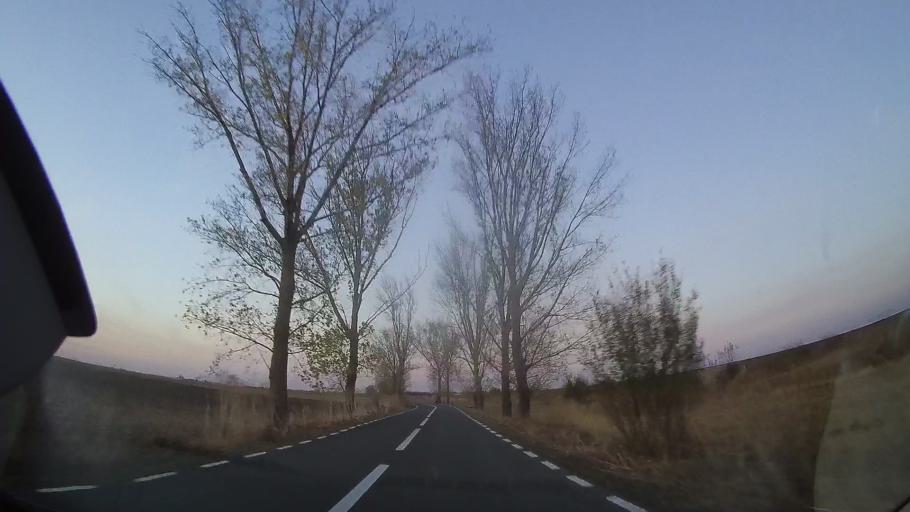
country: RO
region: Constanta
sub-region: Comuna Cobadin
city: Cobadin
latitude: 44.0388
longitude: 28.2578
